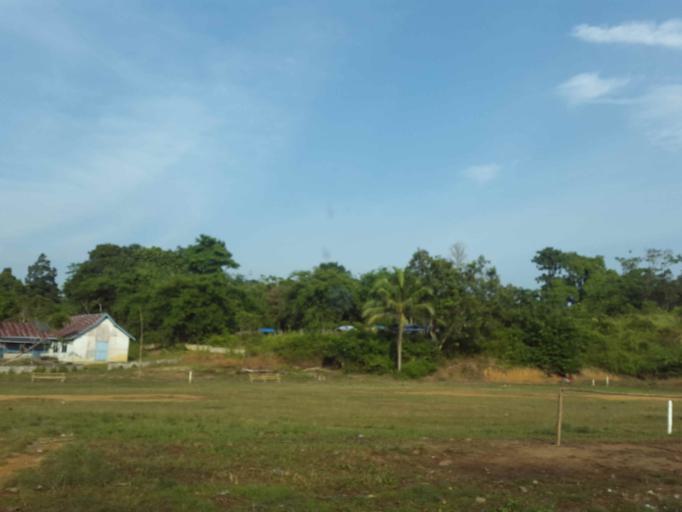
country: MY
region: Sarawak
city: Kuching
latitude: 0.8141
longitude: 110.3439
